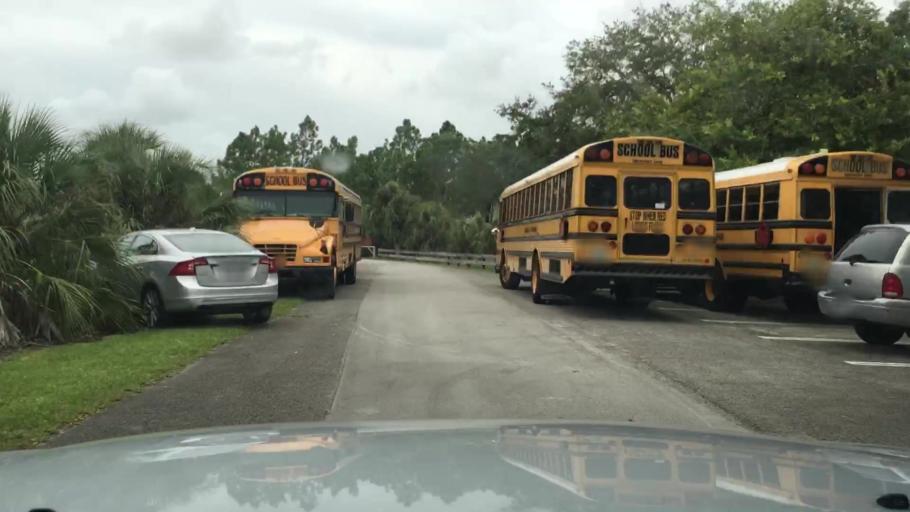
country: US
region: Florida
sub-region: Miami-Dade County
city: South Miami Heights
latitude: 25.5996
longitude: -80.4045
